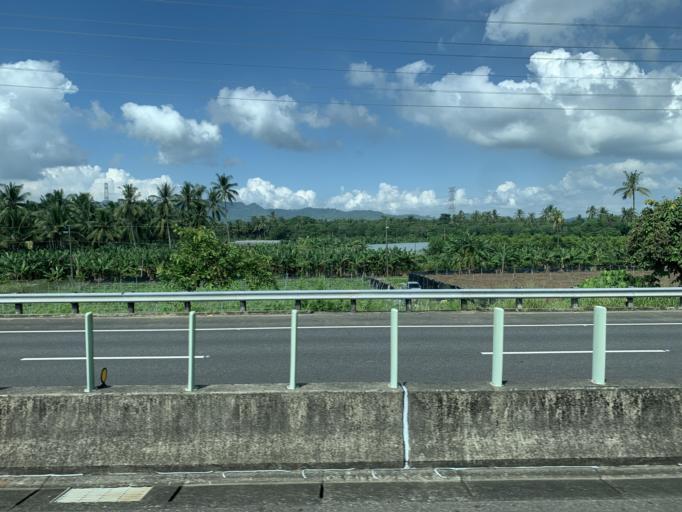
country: TW
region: Taiwan
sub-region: Pingtung
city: Pingtung
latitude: 22.8392
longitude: 120.4954
